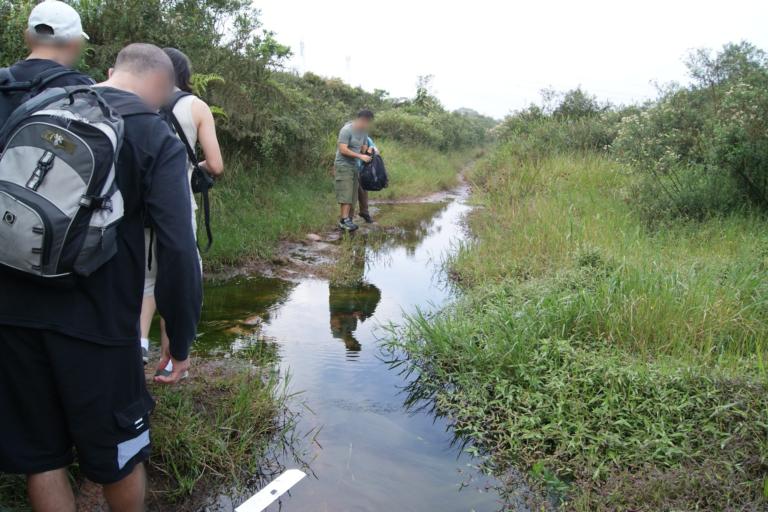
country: BR
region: Sao Paulo
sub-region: Rio Grande Da Serra
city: Rio Grande da Serra
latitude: -23.7732
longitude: -46.3651
